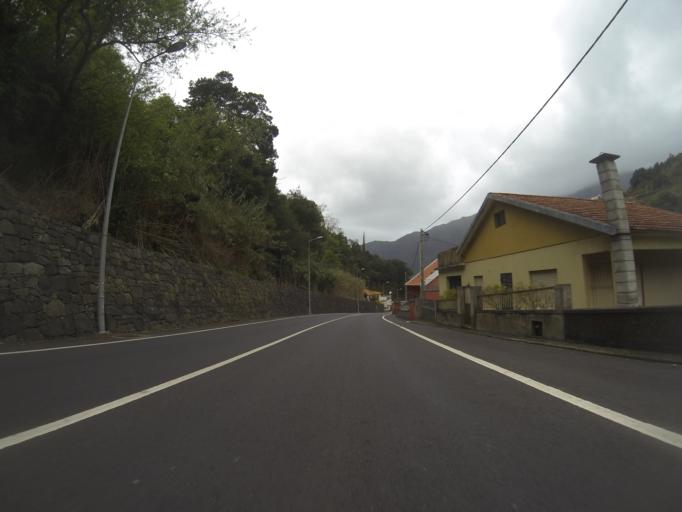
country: PT
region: Madeira
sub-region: Sao Vicente
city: Sao Vicente
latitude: 32.7797
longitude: -17.0331
